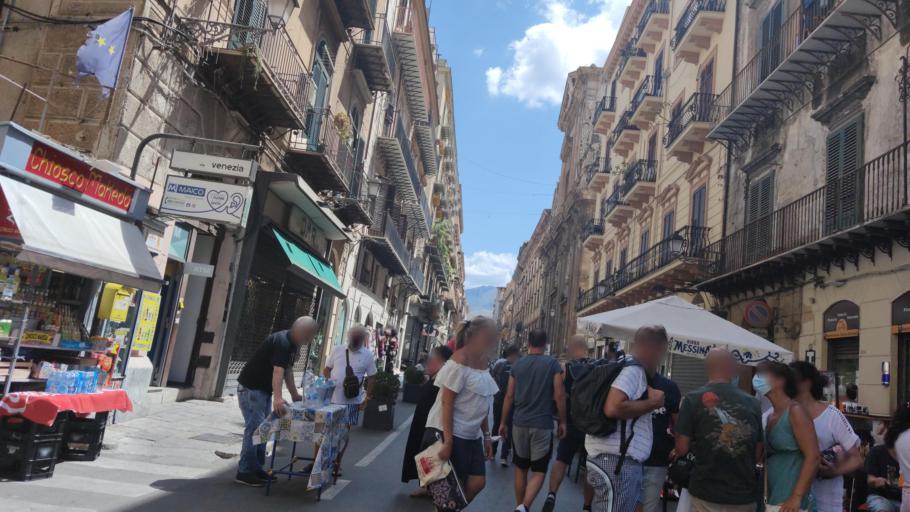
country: IT
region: Sicily
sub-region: Palermo
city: Palermo
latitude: 38.1172
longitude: 13.3605
